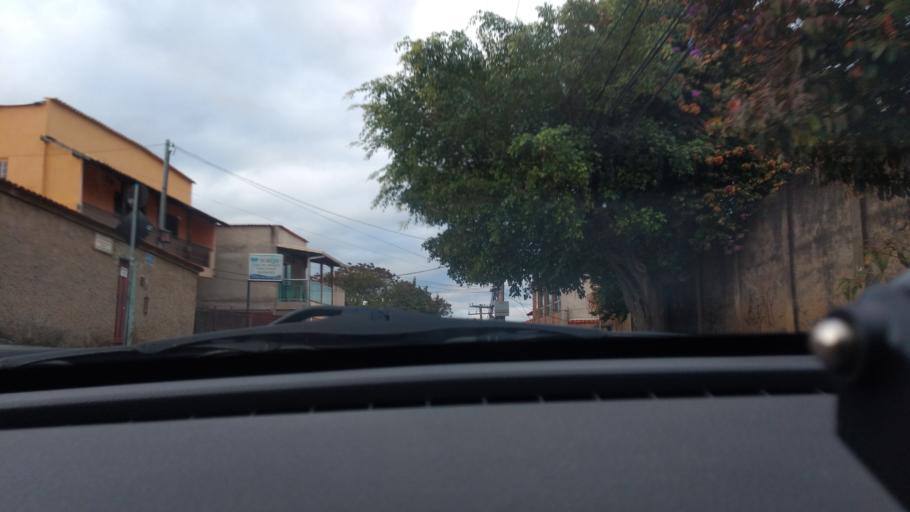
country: BR
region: Minas Gerais
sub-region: Santa Luzia
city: Santa Luzia
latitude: -19.8129
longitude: -43.9388
